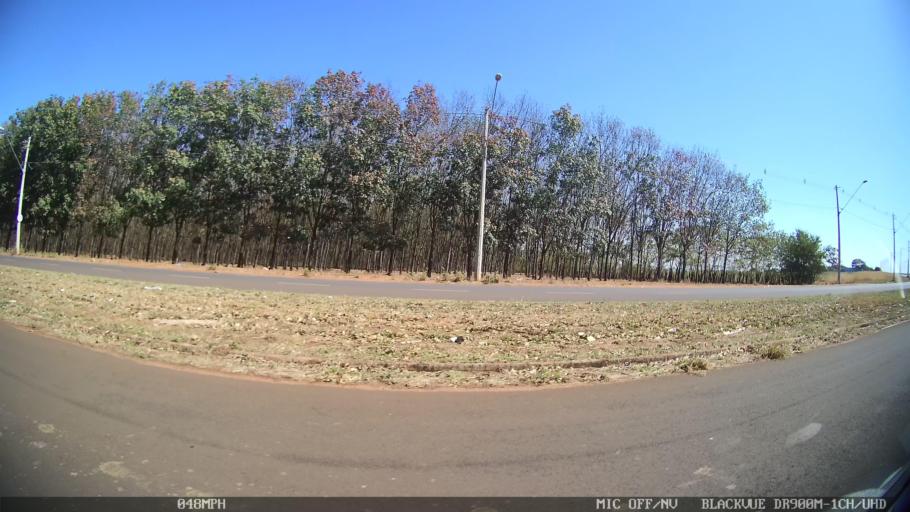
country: BR
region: Sao Paulo
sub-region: Sao Jose Do Rio Preto
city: Sao Jose do Rio Preto
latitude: -20.7348
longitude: -49.4357
